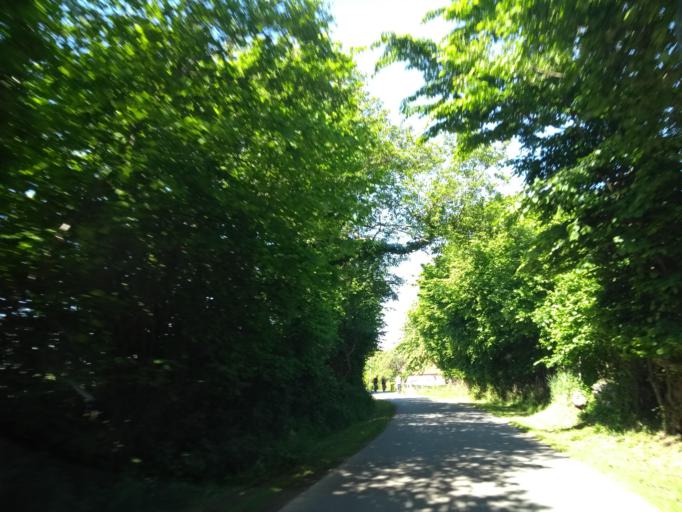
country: DE
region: Schleswig-Holstein
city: Waabs
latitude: 54.5493
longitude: 9.9754
